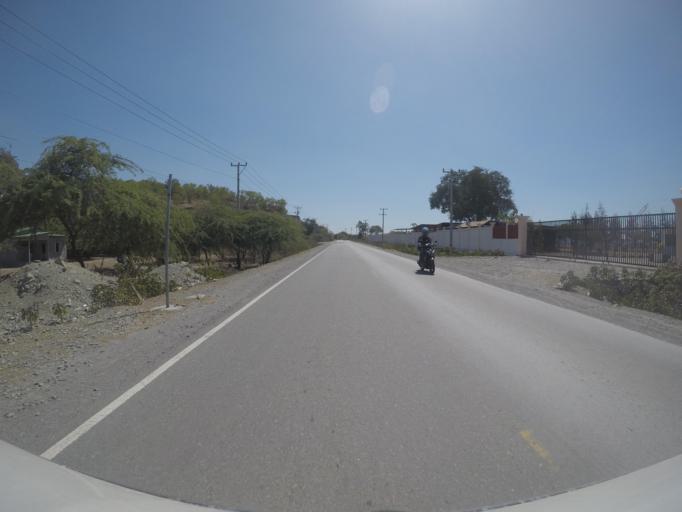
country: TL
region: Liquica
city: Liquica
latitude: -8.5643
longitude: 125.4115
